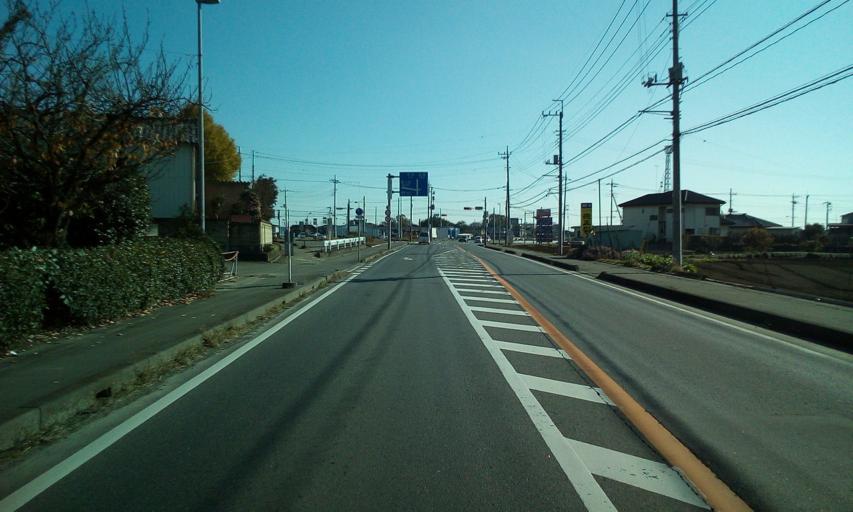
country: JP
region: Ibaraki
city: Sakai
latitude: 36.1325
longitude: 139.7697
